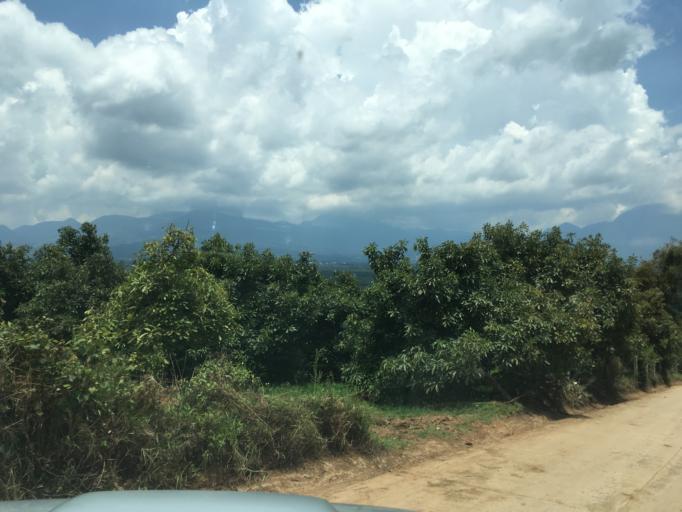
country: MX
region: Michoacan
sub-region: Zitacuaro
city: La Fundicion (Quinta Manzana)
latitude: 19.4886
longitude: -100.3115
